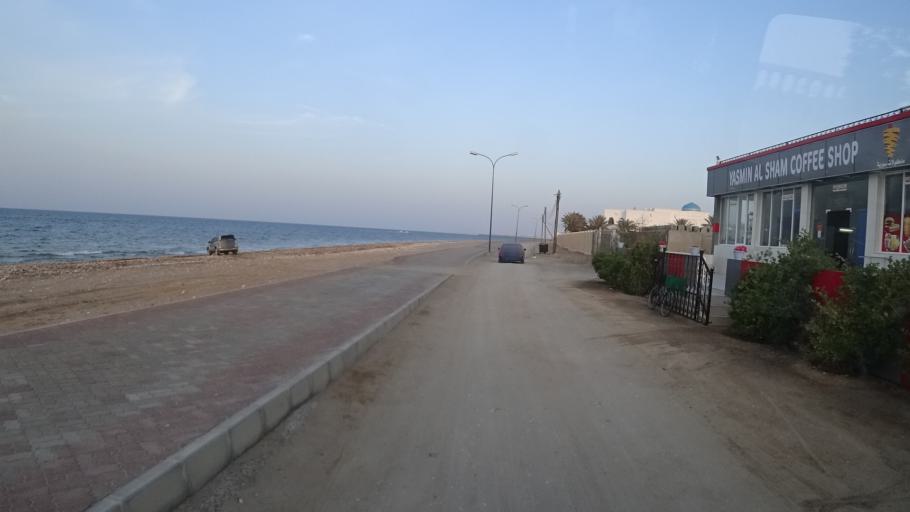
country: OM
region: Ash Sharqiyah
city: Sur
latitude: 22.5922
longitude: 59.5012
